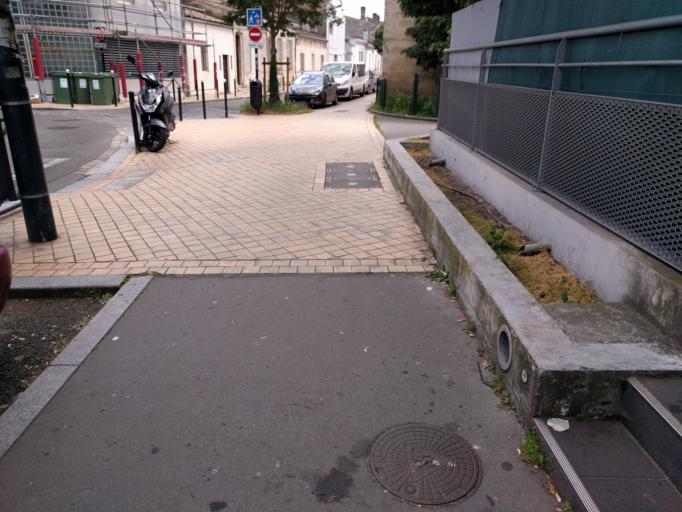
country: FR
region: Aquitaine
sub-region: Departement de la Gironde
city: Bordeaux
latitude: 44.8242
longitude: -0.5770
